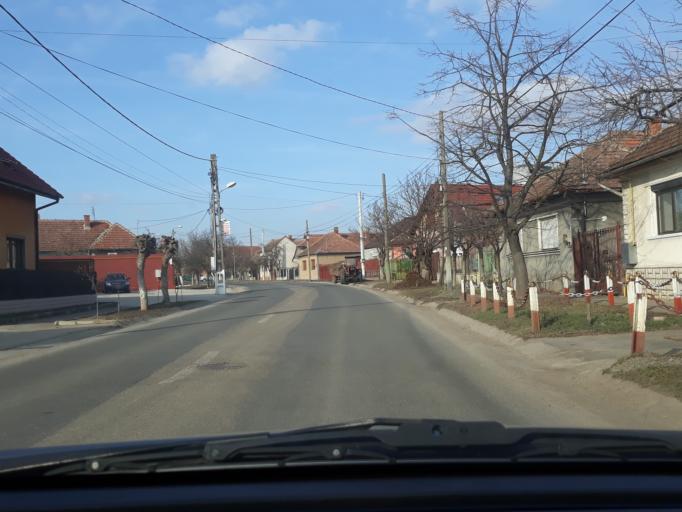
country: RO
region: Bihor
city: Margita
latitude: 47.3520
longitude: 22.3390
